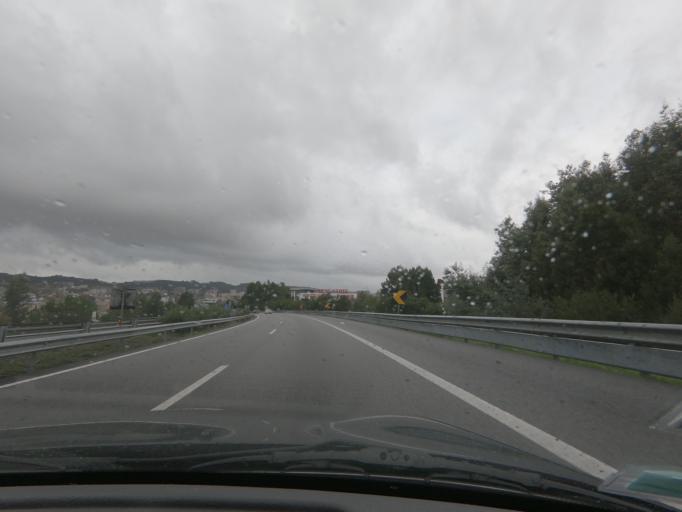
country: PT
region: Porto
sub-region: Valongo
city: Valongo
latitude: 41.1961
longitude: -8.4869
